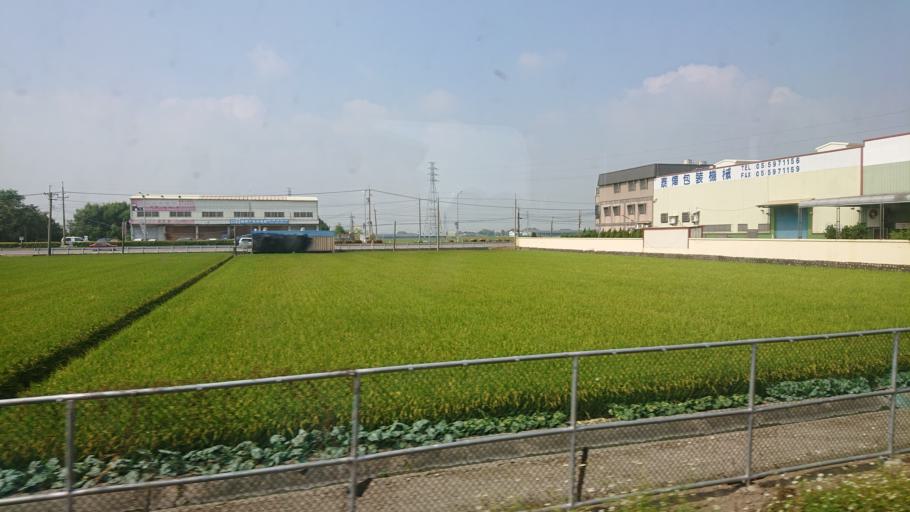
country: TW
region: Taiwan
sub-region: Yunlin
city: Douliu
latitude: 23.6451
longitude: 120.4718
